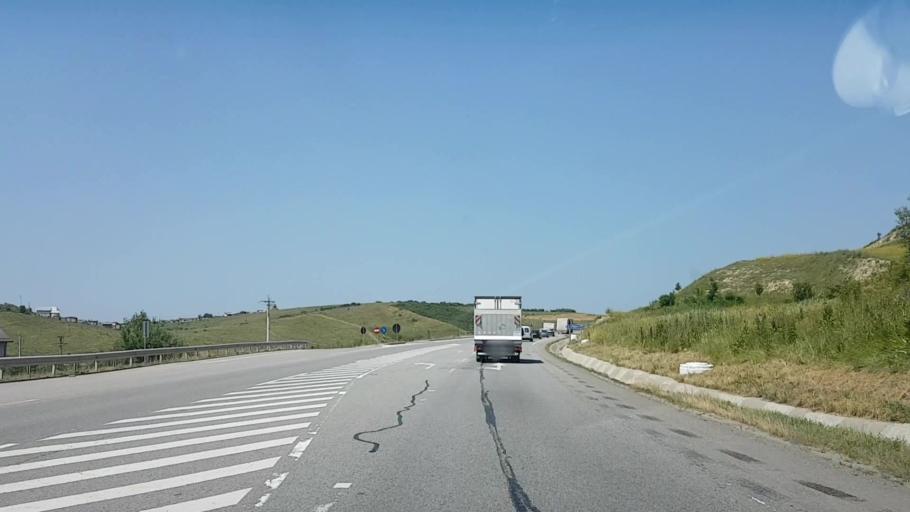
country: RO
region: Cluj
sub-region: Comuna Apahida
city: Dezmir
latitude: 46.7668
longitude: 23.6903
